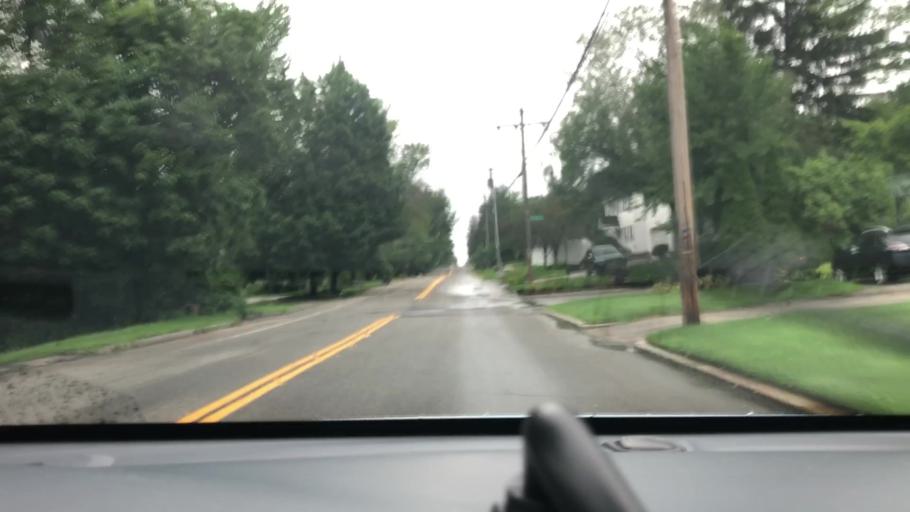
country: US
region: New Hampshire
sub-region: Merrimack County
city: South Hooksett
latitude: 43.0258
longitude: -71.4625
